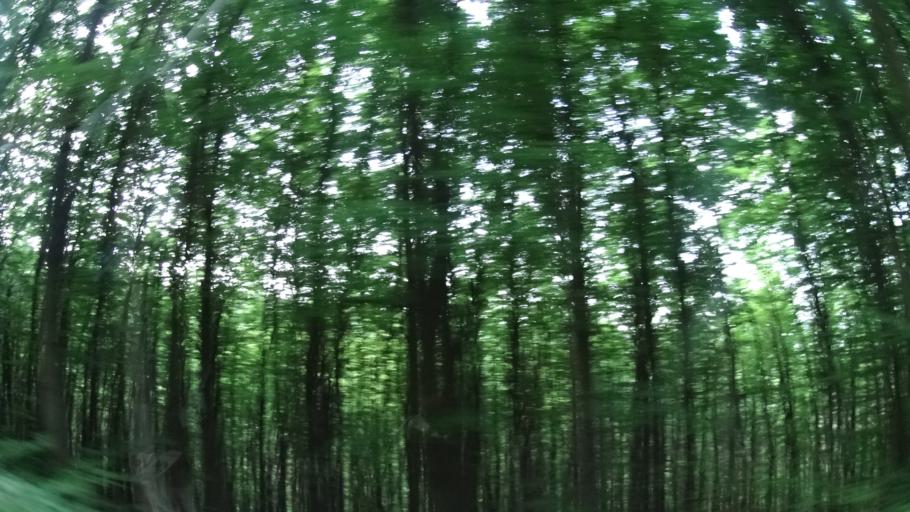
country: DE
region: Hesse
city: Michelstadt
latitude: 49.6721
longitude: 9.0547
